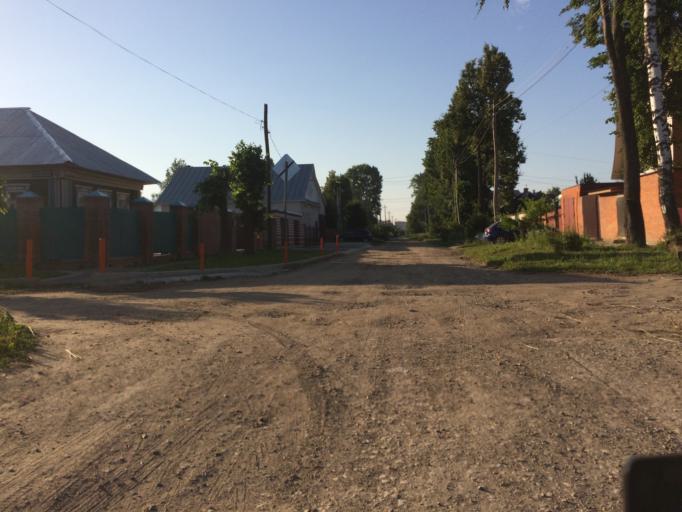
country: RU
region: Mariy-El
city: Yoshkar-Ola
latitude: 56.6502
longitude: 47.9075
